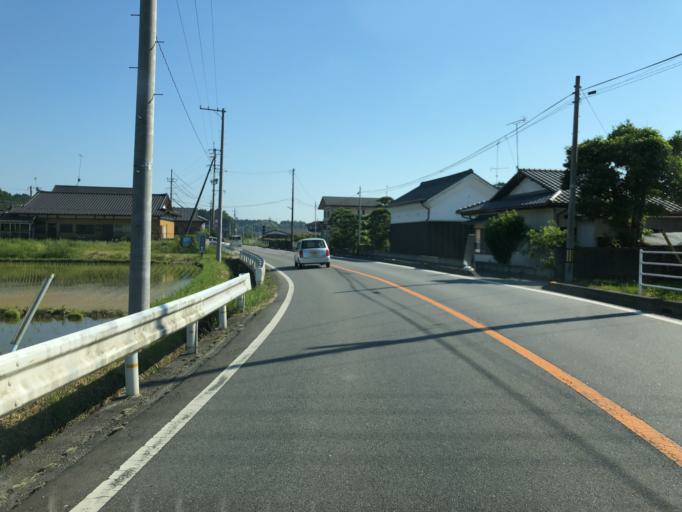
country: JP
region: Fukushima
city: Iwaki
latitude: 36.9351
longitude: 140.7981
